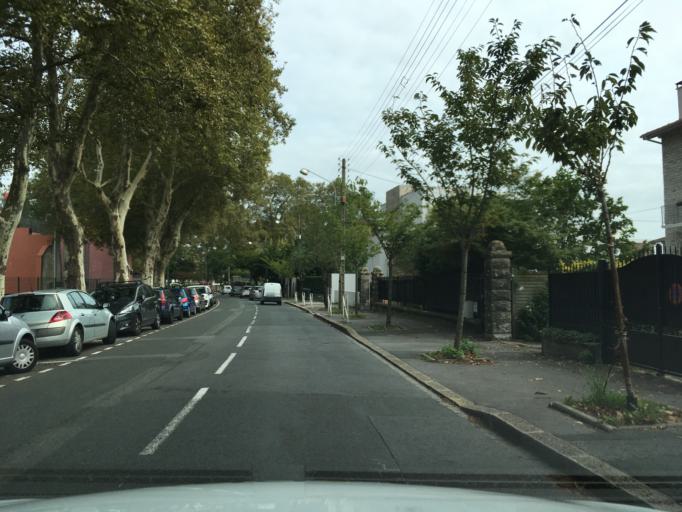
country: FR
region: Aquitaine
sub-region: Departement des Pyrenees-Atlantiques
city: Bayonne
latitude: 43.4847
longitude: -1.4781
